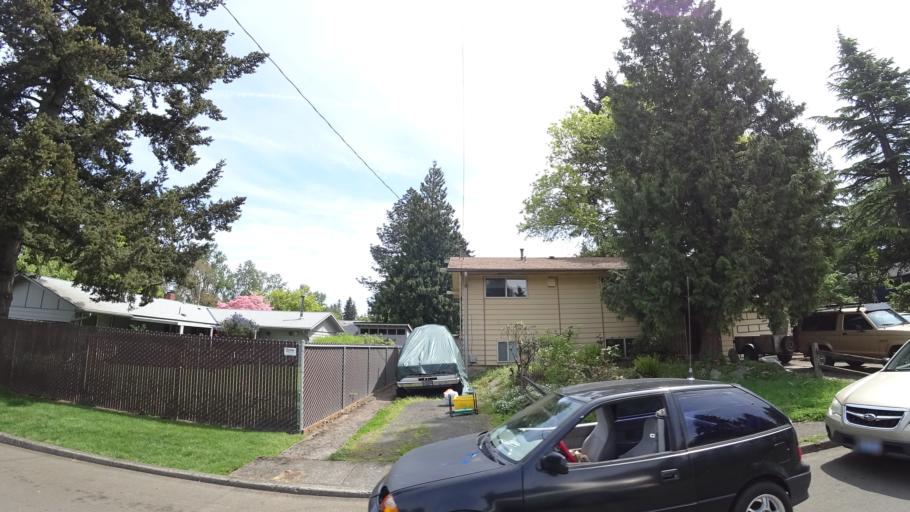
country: US
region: Oregon
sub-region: Clackamas County
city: Milwaukie
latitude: 45.4579
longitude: -122.6141
